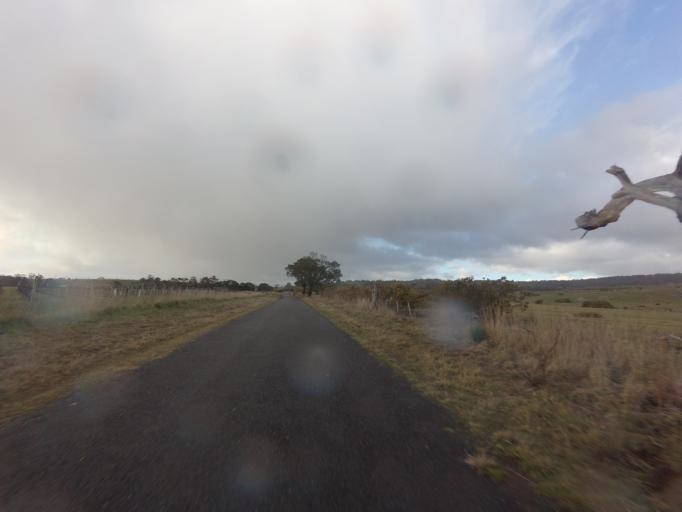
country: AU
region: Tasmania
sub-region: Break O'Day
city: St Helens
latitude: -42.0015
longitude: 148.0870
